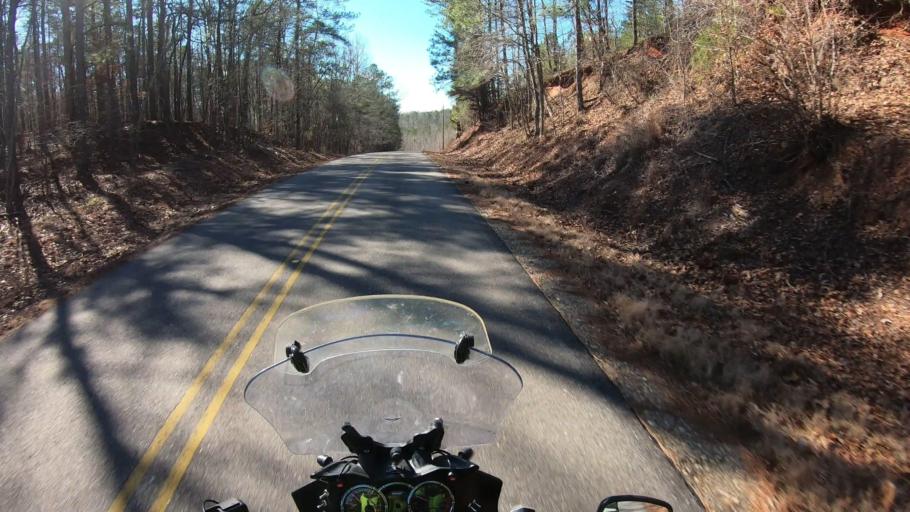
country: US
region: Alabama
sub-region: Clay County
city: Lineville
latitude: 33.4524
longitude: -85.7359
